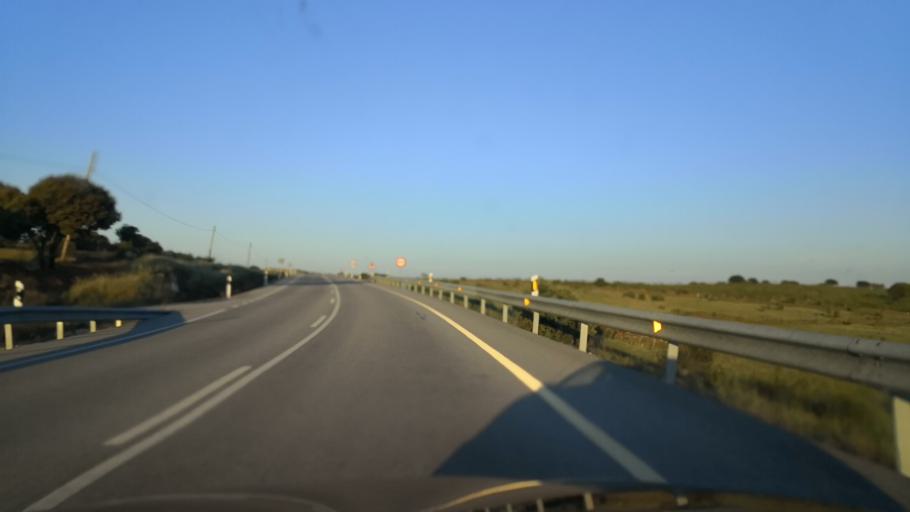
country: ES
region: Extremadura
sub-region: Provincia de Caceres
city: Salorino
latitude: 39.5133
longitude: -7.0656
